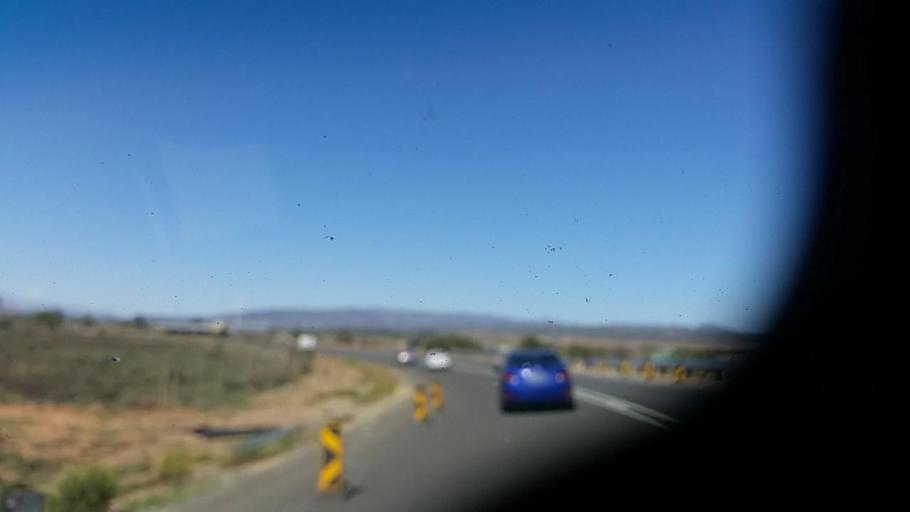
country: ZA
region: Western Cape
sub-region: Eden District Municipality
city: Oudtshoorn
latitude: -33.5858
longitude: 22.2944
